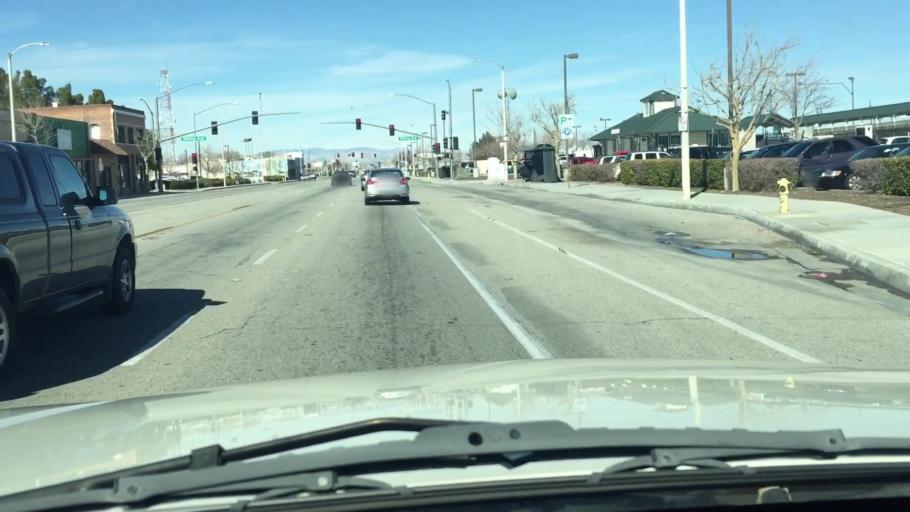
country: US
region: California
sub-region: Los Angeles County
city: Lancaster
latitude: 34.6956
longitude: -118.1364
